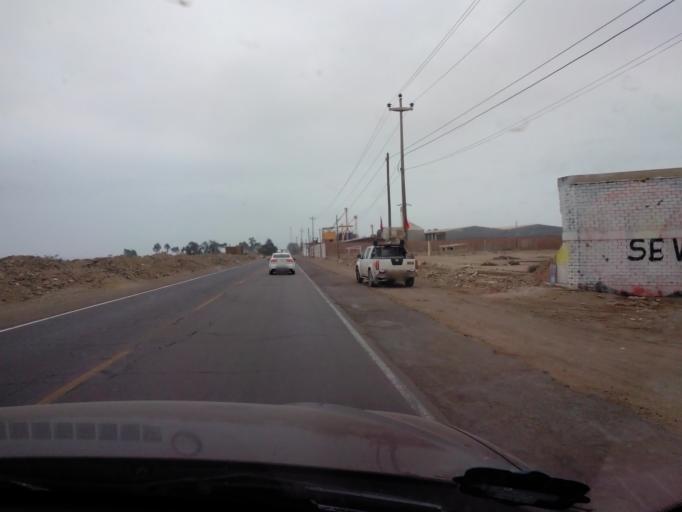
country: PE
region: Ica
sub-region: Provincia de Chincha
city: San Pedro
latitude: -13.4108
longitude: -76.1738
